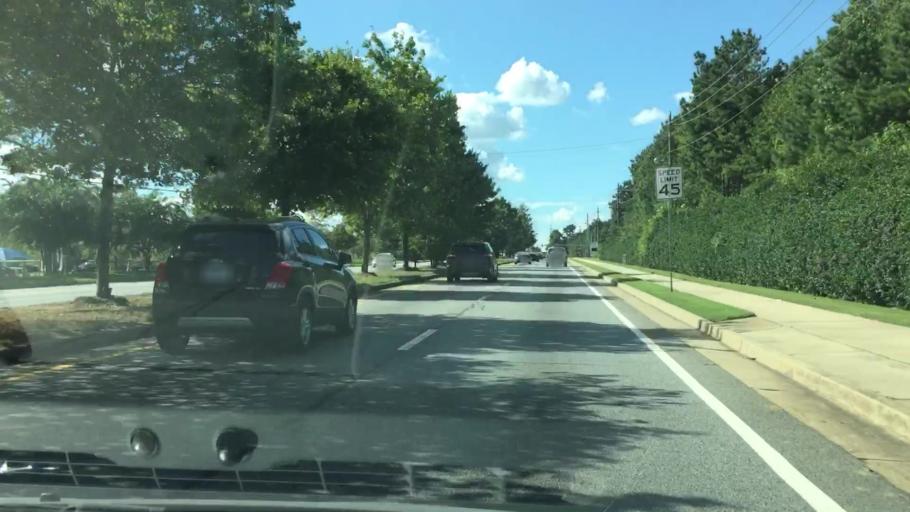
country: US
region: Georgia
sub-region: Cobb County
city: Austell
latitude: 33.8617
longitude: -84.6203
